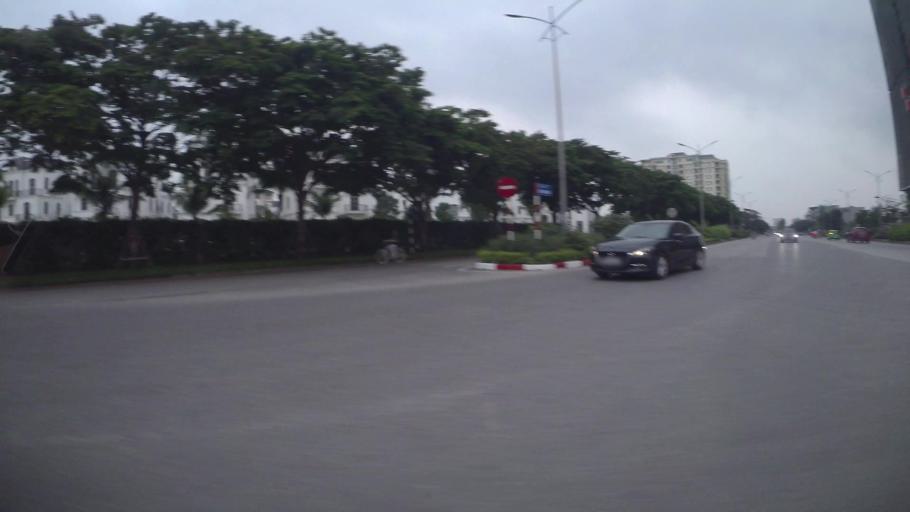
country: VN
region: Ha Noi
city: Trau Quy
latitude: 21.0424
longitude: 105.9059
